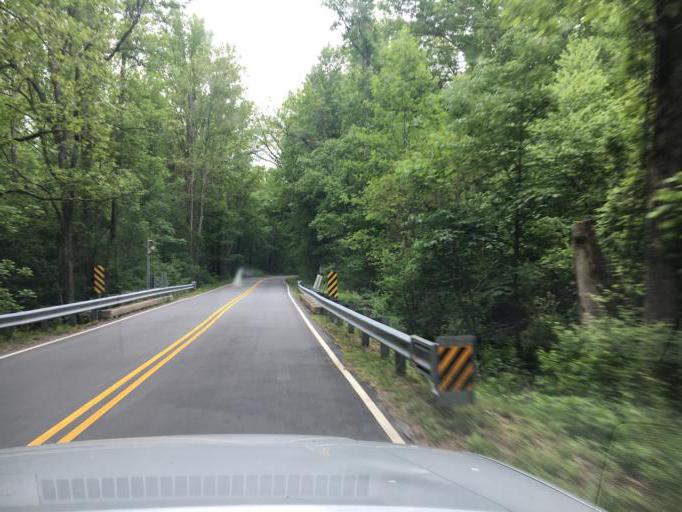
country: US
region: South Carolina
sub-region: Greenville County
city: Tigerville
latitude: 35.1705
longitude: -82.4028
